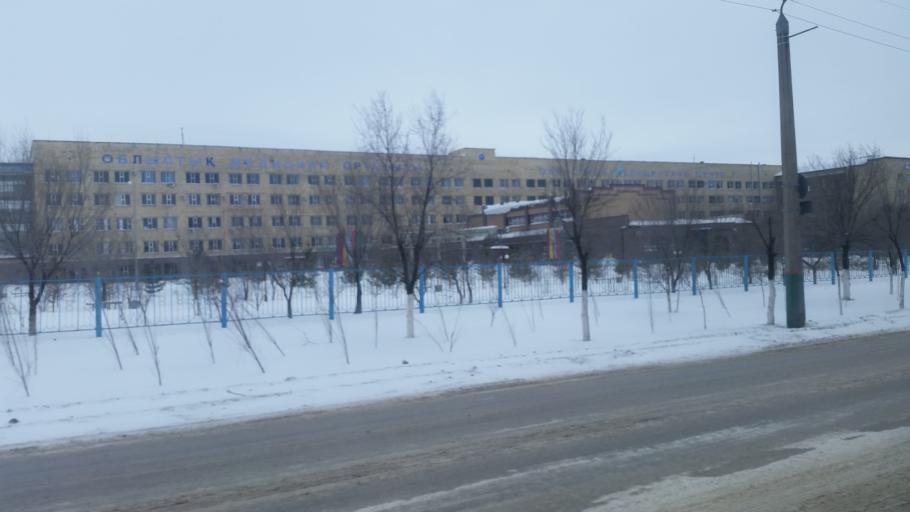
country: KZ
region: Qaraghandy
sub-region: Qaraghandy Qalasy
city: Karagandy
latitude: 49.7730
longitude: 73.1472
